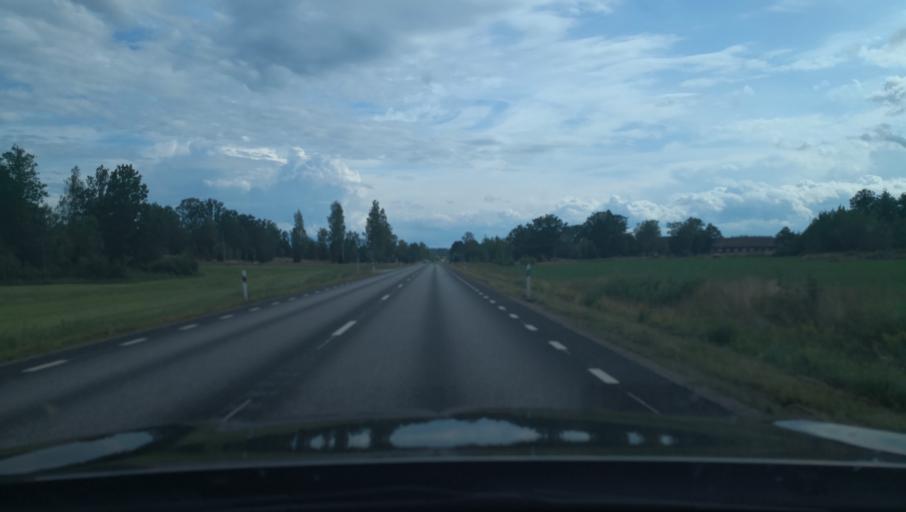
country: SE
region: Kalmar
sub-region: Vimmerby Kommun
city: Sodra Vi
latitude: 57.8169
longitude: 15.7552
